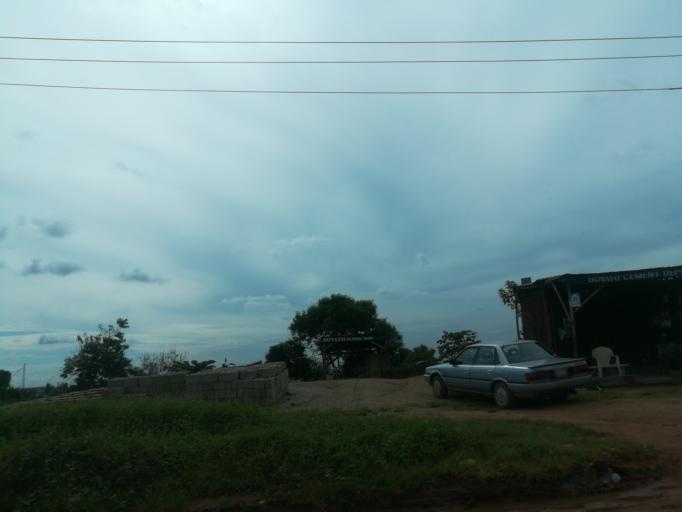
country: NG
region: Oyo
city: Ibadan
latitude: 7.3780
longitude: 3.9727
